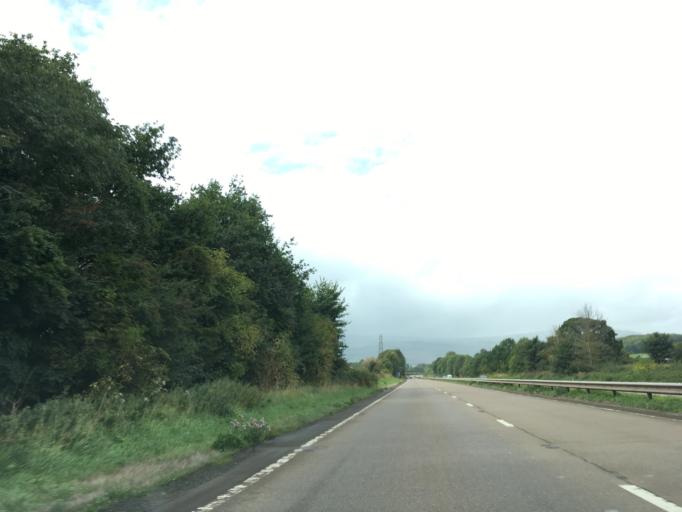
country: GB
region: Wales
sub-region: Monmouthshire
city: Llanarth
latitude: 51.7843
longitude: -2.9602
